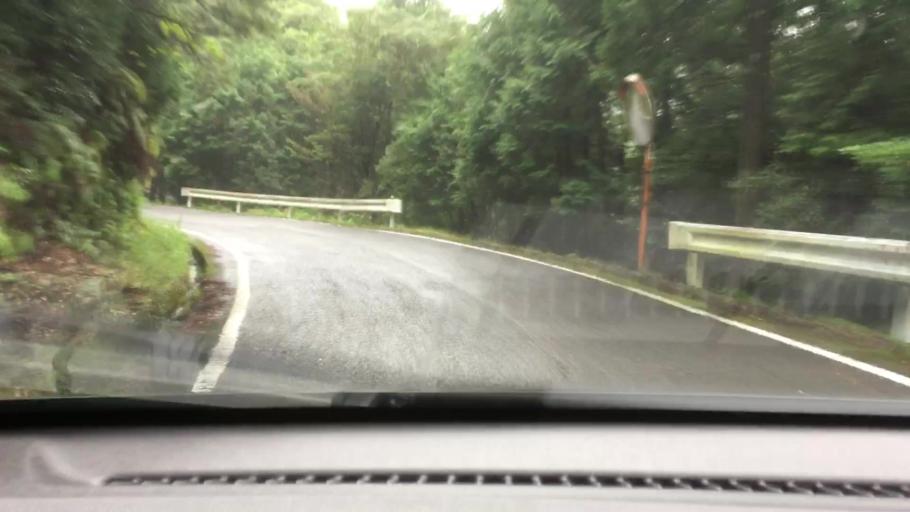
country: JP
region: Nagasaki
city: Togitsu
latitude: 32.9202
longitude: 129.7270
